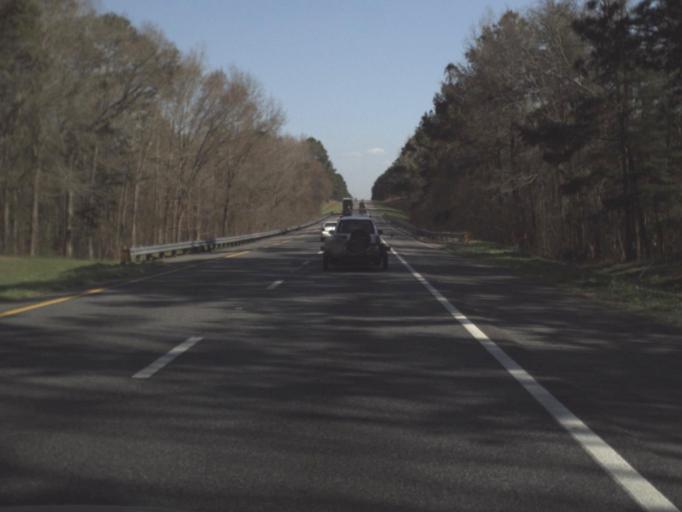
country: US
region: Florida
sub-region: Gadsden County
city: Midway
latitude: 30.5253
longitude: -84.4987
